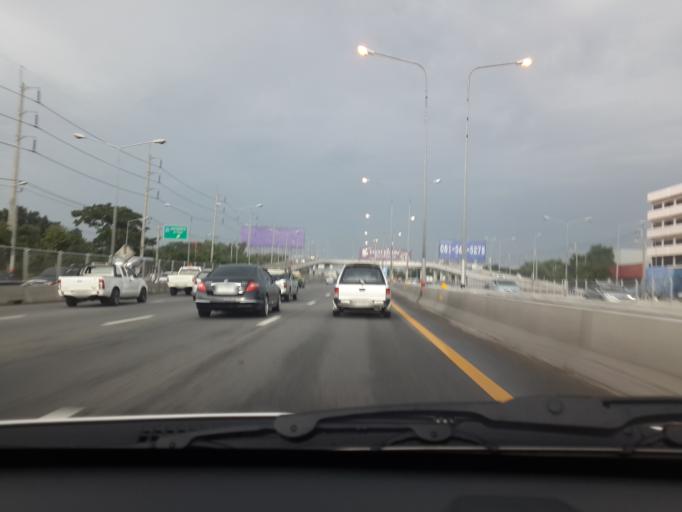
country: TH
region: Bangkok
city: Suan Luang
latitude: 13.7387
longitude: 100.6547
